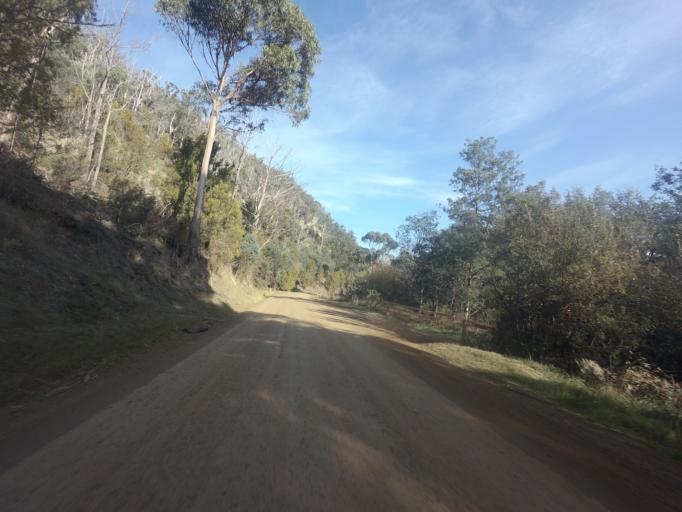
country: AU
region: Tasmania
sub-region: Sorell
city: Sorell
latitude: -42.4949
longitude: 147.4335
